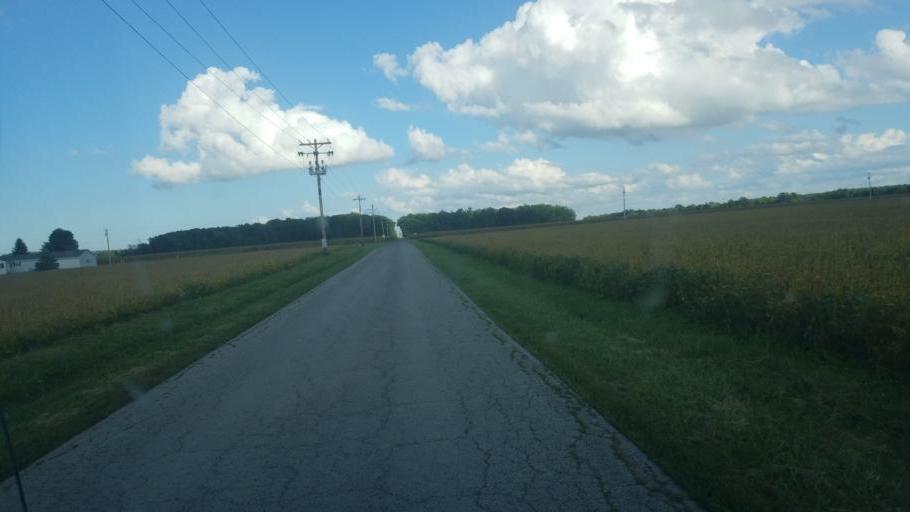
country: US
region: Ohio
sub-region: Hancock County
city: Arlington
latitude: 40.9363
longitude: -83.7300
